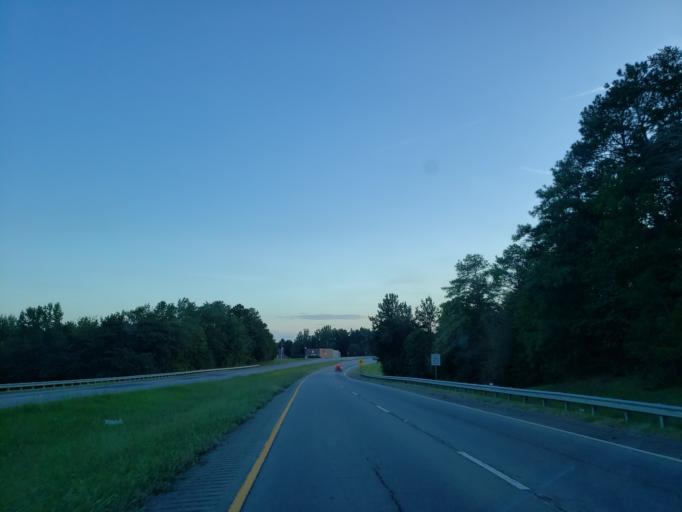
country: US
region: Georgia
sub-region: Floyd County
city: Lindale
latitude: 34.2025
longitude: -85.1944
